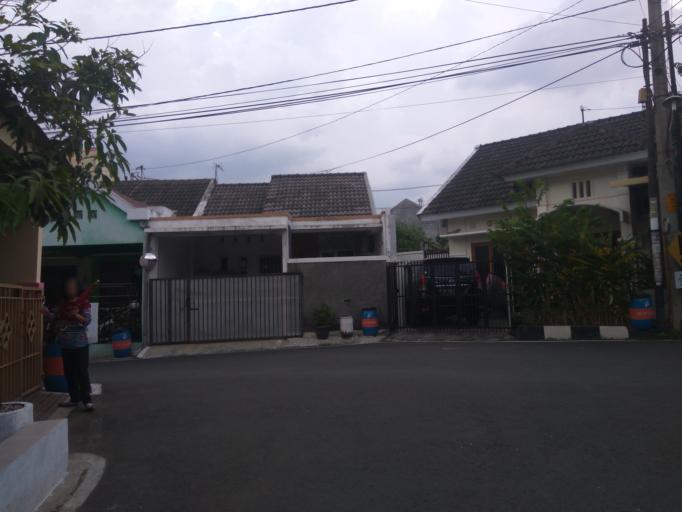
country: ID
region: Central Java
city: Semarang
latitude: -7.0663
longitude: 110.4452
